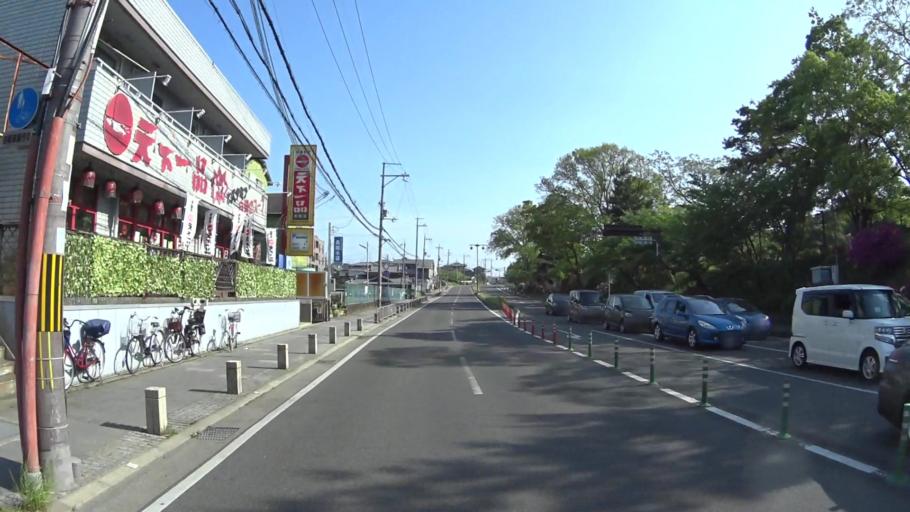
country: JP
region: Kyoto
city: Muko
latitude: 34.9237
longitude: 135.6890
